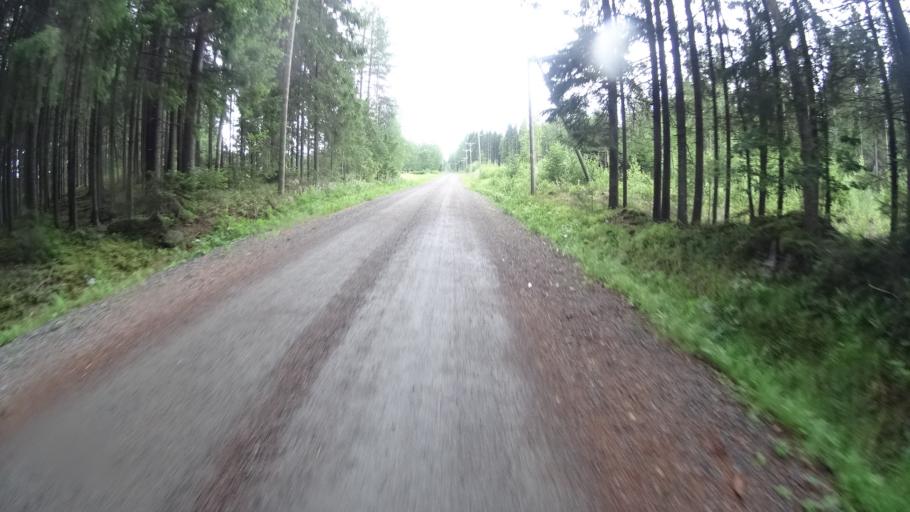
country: FI
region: Uusimaa
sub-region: Helsinki
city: Karkkila
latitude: 60.5925
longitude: 24.1589
